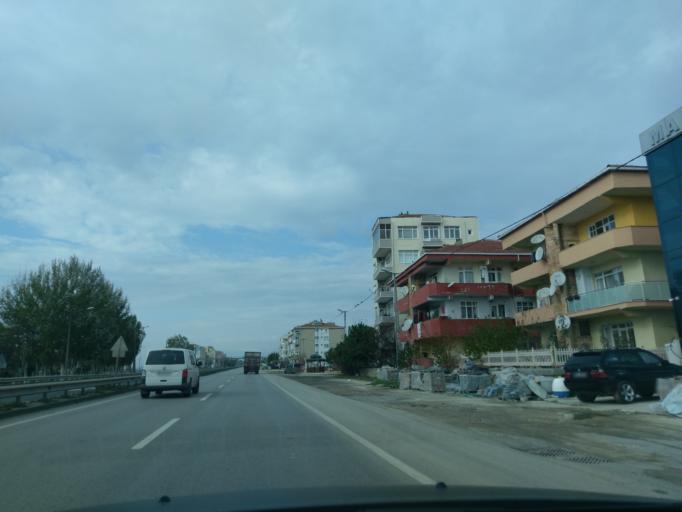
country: TR
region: Istanbul
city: Celaliye
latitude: 41.0447
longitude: 28.4115
